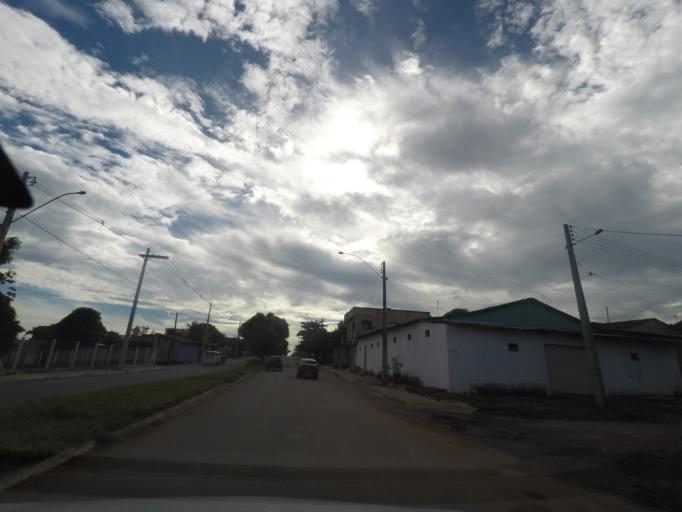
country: BR
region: Goias
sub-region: Aparecida De Goiania
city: Aparecida de Goiania
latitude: -16.8170
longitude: -49.3196
